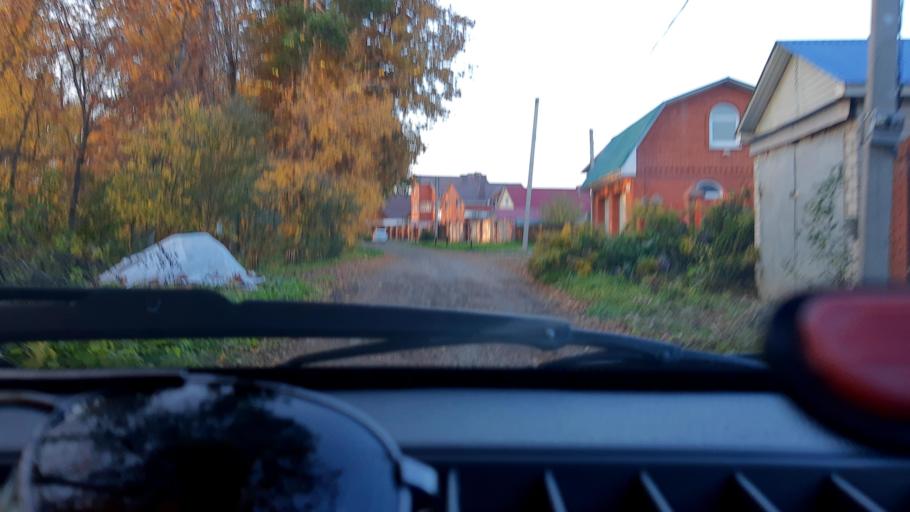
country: RU
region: Bashkortostan
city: Ufa
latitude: 54.7848
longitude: 55.9460
